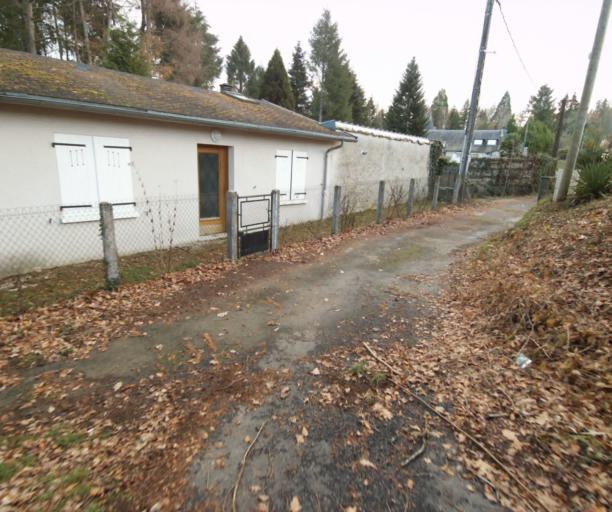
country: FR
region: Limousin
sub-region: Departement de la Correze
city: Laguenne
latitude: 45.2303
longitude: 1.7804
